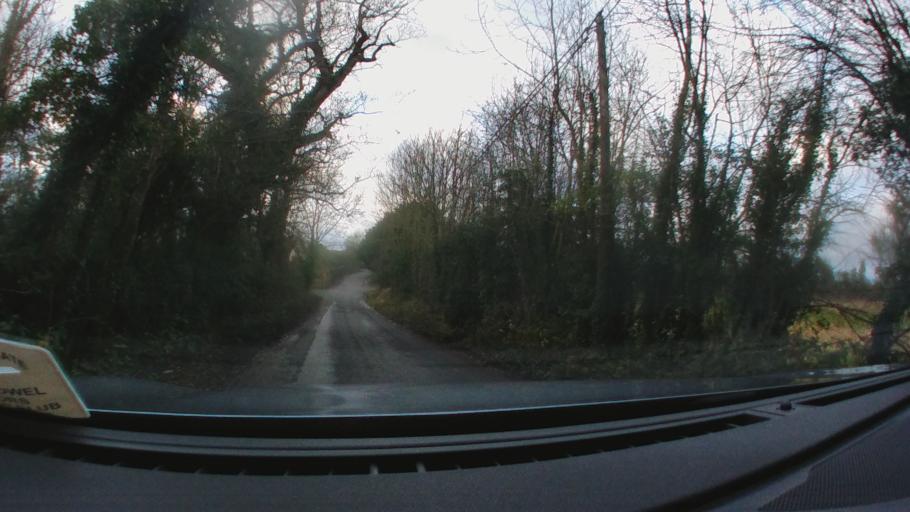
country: IE
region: Leinster
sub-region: Kilkenny
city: Thomastown
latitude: 52.5555
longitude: -7.1227
